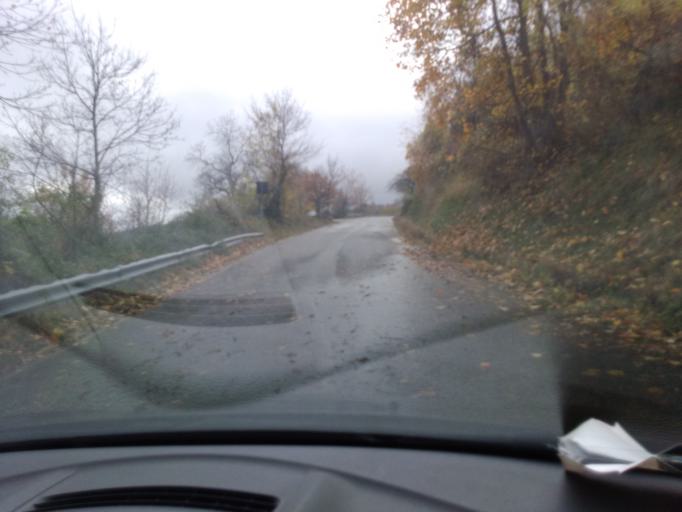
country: IT
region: Latium
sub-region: Provincia di Rieti
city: Accumoli
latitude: 42.6944
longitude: 13.2061
